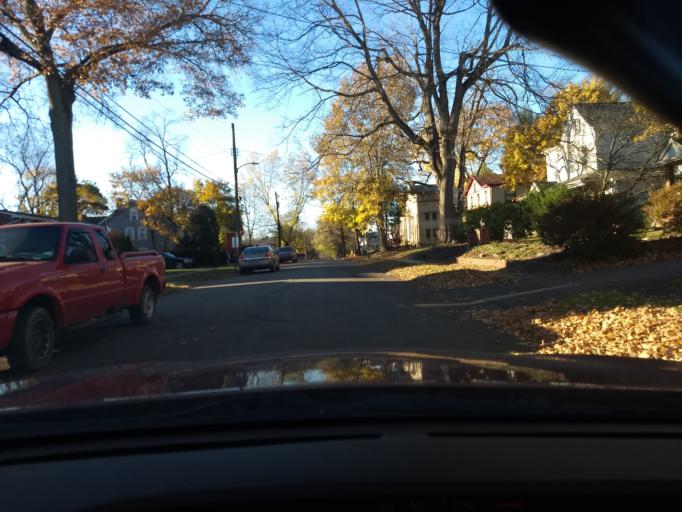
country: US
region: Pennsylvania
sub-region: Allegheny County
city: Oakdale
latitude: 40.3987
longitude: -80.1834
